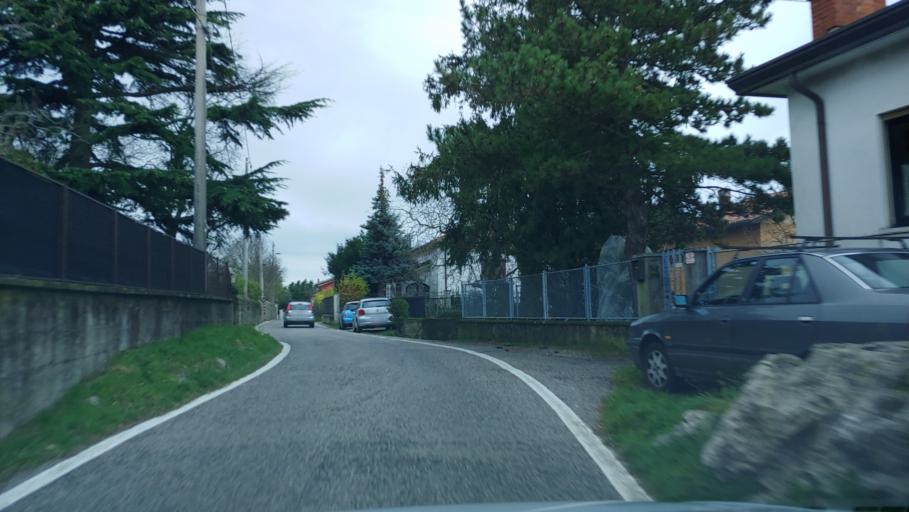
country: IT
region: Friuli Venezia Giulia
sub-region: Provincia di Trieste
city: Prosecco-Contovello
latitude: 45.7071
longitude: 13.7312
